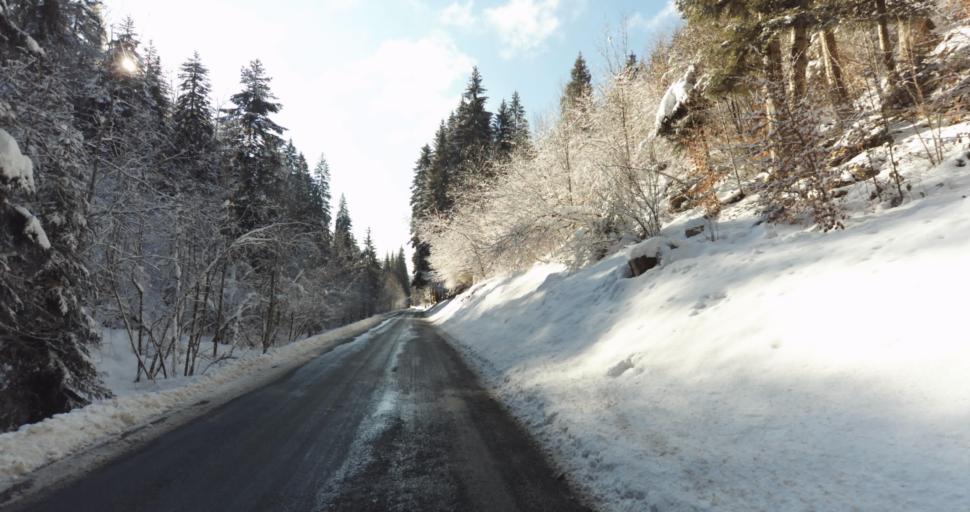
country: FR
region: Rhone-Alpes
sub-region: Departement de l'Ain
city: Nantua
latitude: 46.1727
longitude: 5.6404
